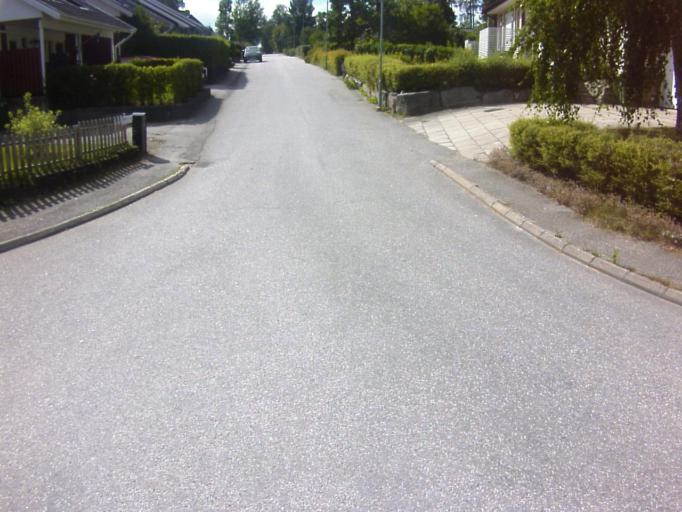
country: SE
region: Soedermanland
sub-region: Eskilstuna Kommun
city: Hallbybrunn
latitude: 59.3448
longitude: 16.4350
